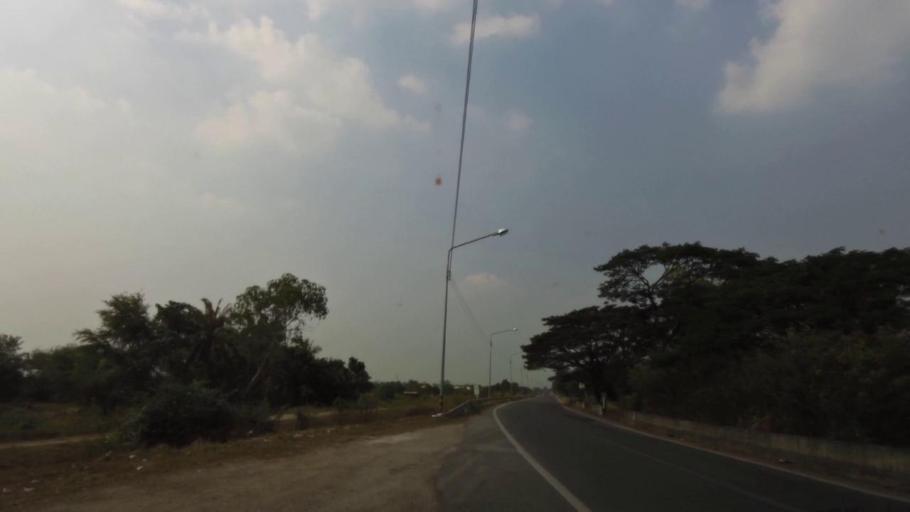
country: TH
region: Phra Nakhon Si Ayutthaya
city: Phra Nakhon Si Ayutthaya
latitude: 14.3137
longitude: 100.5624
